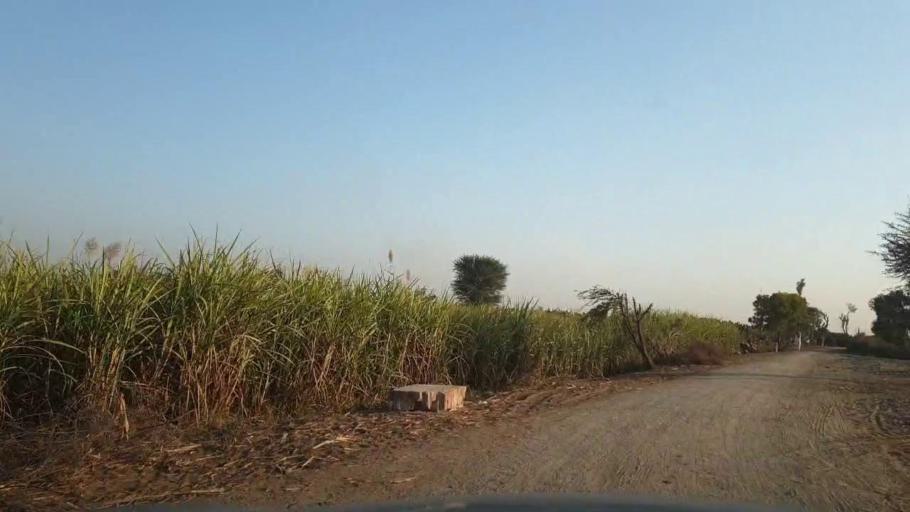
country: PK
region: Sindh
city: Tando Allahyar
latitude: 25.5884
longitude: 68.6981
